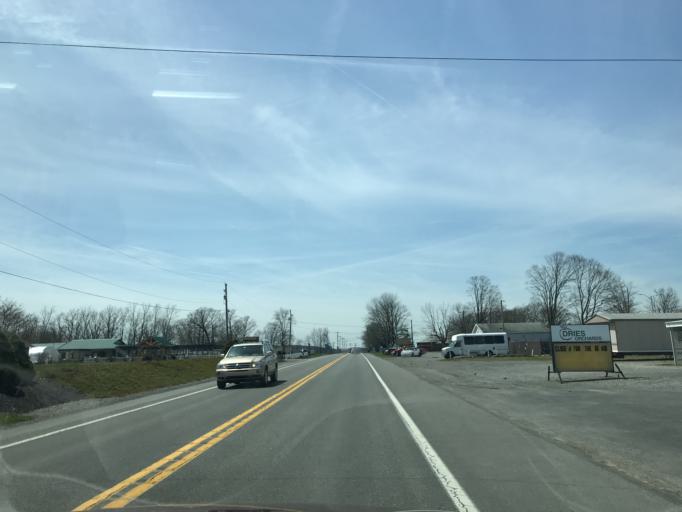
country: US
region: Pennsylvania
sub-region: Snyder County
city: Selinsgrove
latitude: 40.8070
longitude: -76.8801
